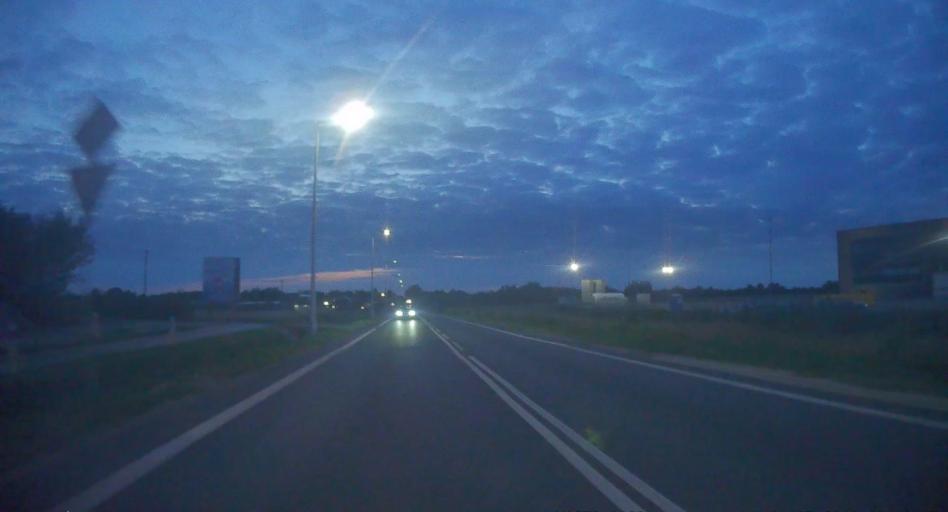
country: PL
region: Silesian Voivodeship
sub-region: Powiat klobucki
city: Kamyk
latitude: 50.8763
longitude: 19.0005
